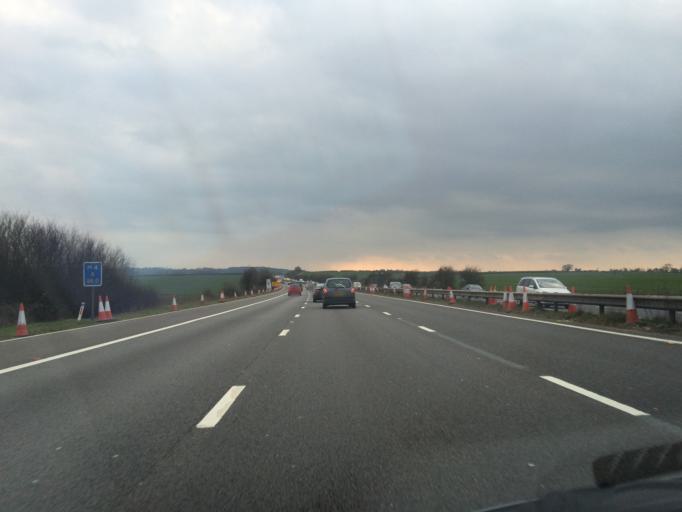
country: GB
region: England
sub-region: West Berkshire
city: Winterbourne
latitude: 51.4555
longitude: -1.3701
